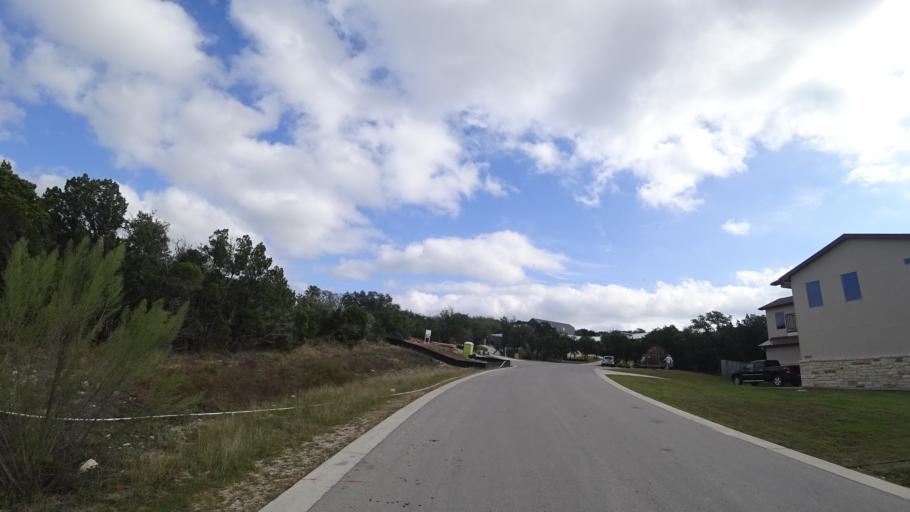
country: US
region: Texas
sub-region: Travis County
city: Bee Cave
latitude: 30.2536
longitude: -97.9258
